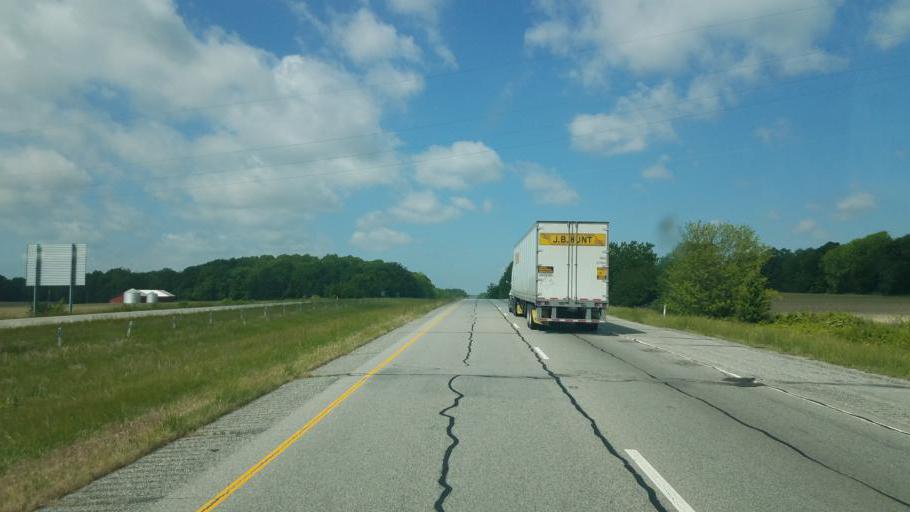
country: US
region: Indiana
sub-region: Vigo County
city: West Terre Haute
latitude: 39.4468
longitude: -87.4835
